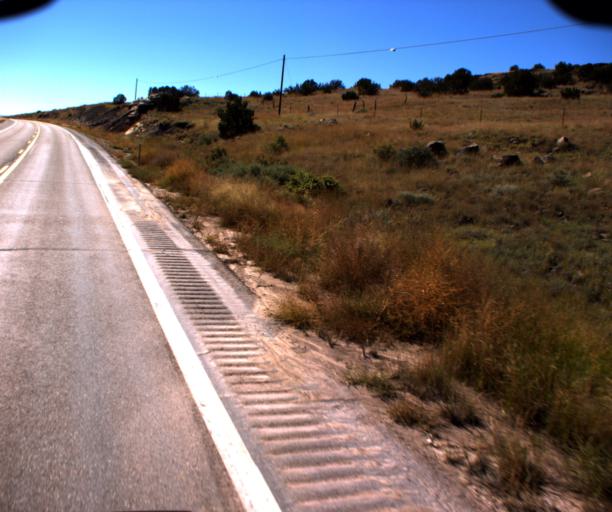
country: US
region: Arizona
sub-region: Apache County
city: Saint Johns
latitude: 34.3302
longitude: -109.3872
